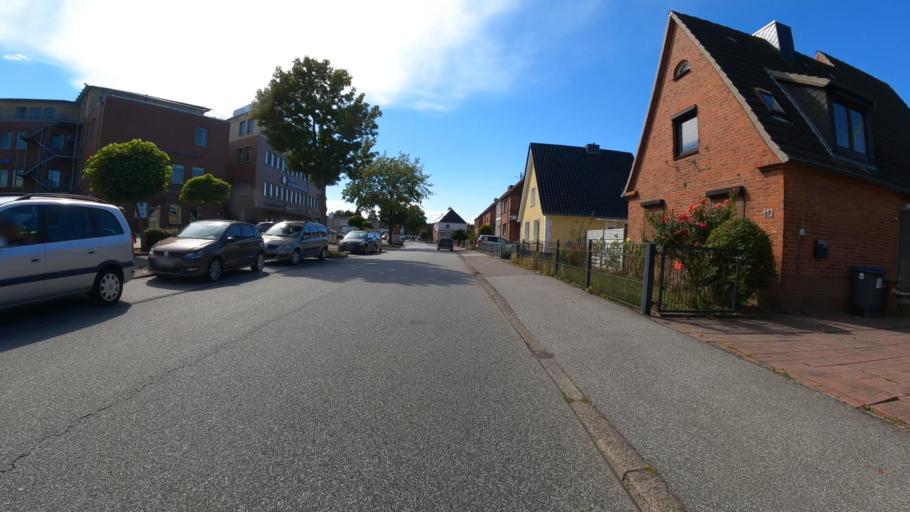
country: DE
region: Schleswig-Holstein
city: Hamberge
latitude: 53.8405
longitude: 10.6313
